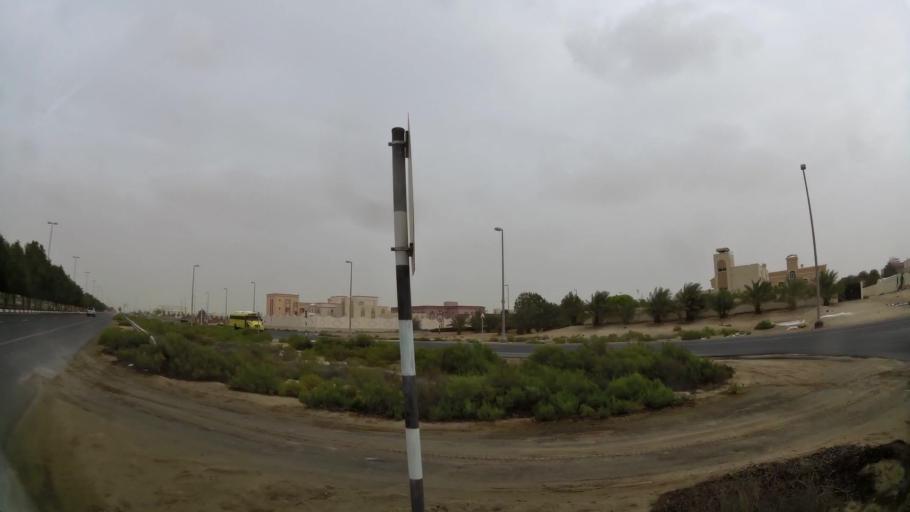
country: AE
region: Abu Dhabi
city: Abu Dhabi
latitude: 24.3816
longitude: 54.6962
